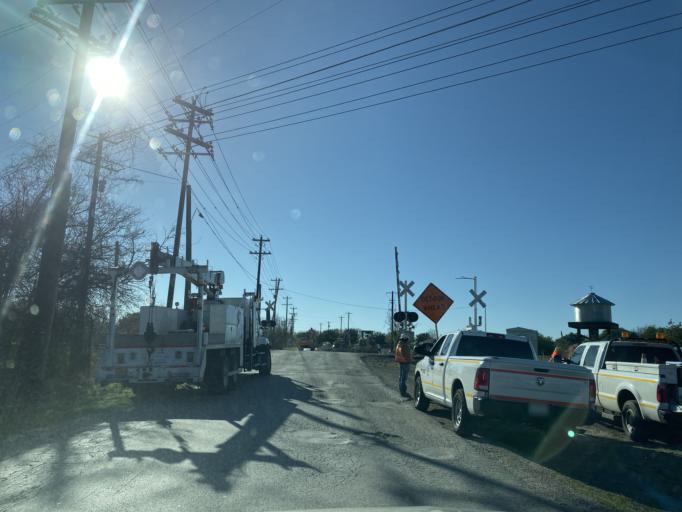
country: US
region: Texas
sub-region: Hays County
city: Kyle
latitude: 30.0004
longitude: -97.8721
